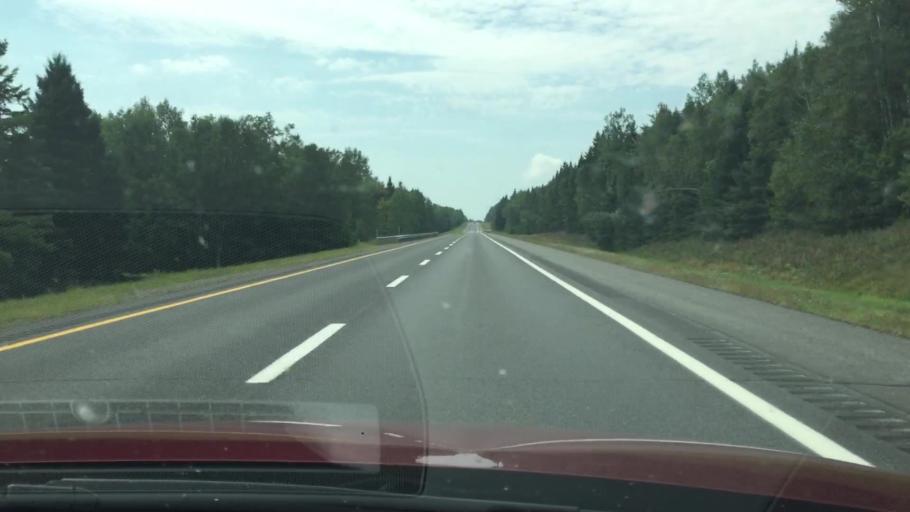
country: US
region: Maine
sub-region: Aroostook County
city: Hodgdon
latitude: 46.1321
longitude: -68.0913
